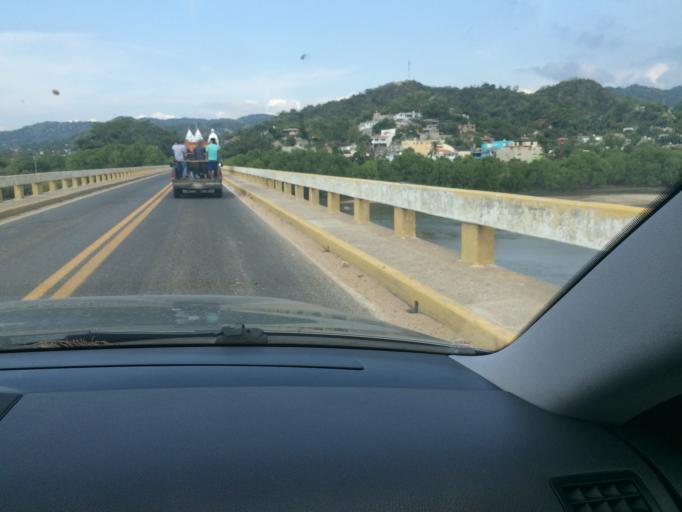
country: MX
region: Jalisco
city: Cihuatlan
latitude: 19.2362
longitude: -104.5534
